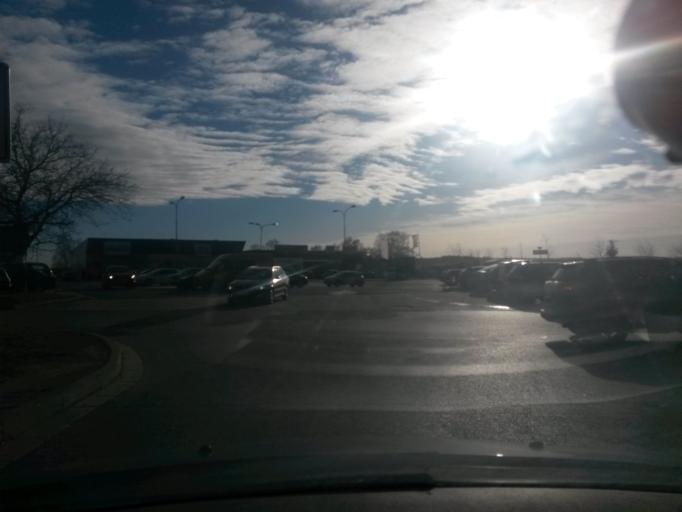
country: CZ
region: Central Bohemia
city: Jesenice
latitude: 49.9658
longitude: 14.5179
